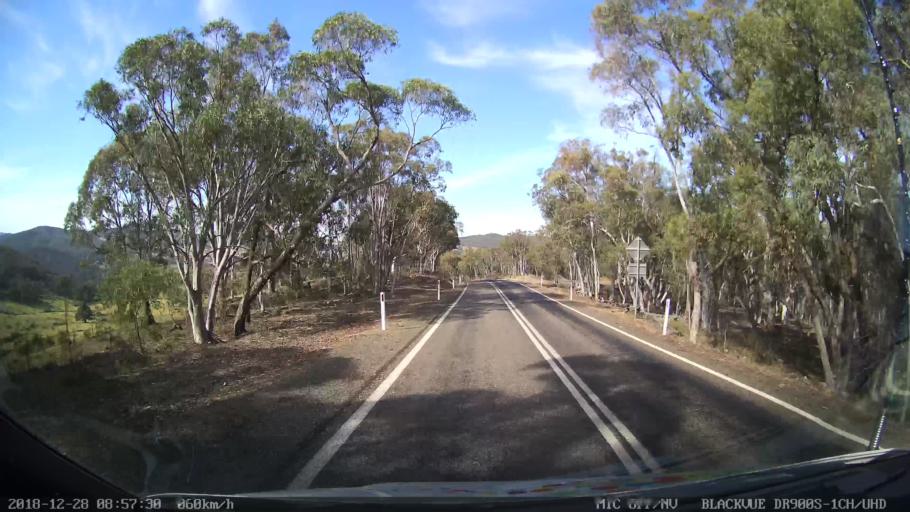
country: AU
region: New South Wales
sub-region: Upper Lachlan Shire
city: Crookwell
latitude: -34.1189
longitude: 149.3349
